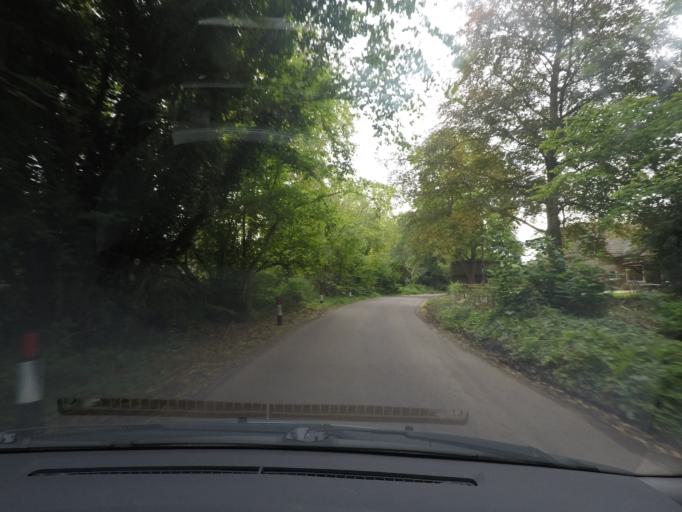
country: GB
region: England
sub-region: Wiltshire
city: Woodborough
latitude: 51.3264
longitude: -1.8021
